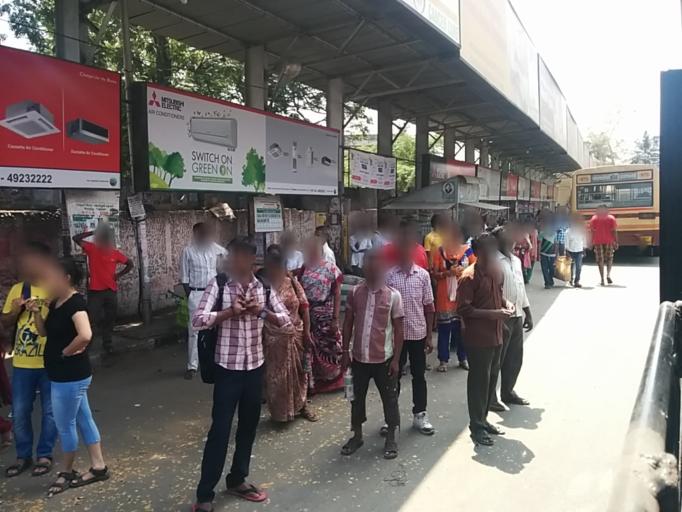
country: IN
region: Tamil Nadu
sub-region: Kancheepuram
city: Alandur
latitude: 13.0225
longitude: 80.2269
